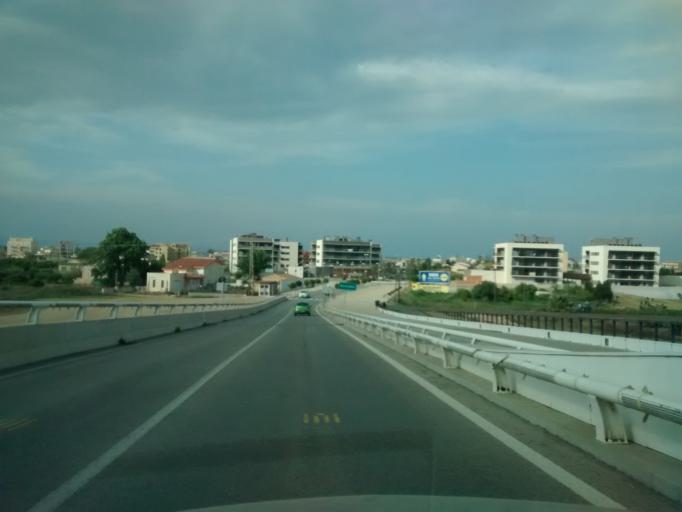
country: ES
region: Catalonia
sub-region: Provincia de Tarragona
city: Deltebre
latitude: 40.7138
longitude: 0.7177
